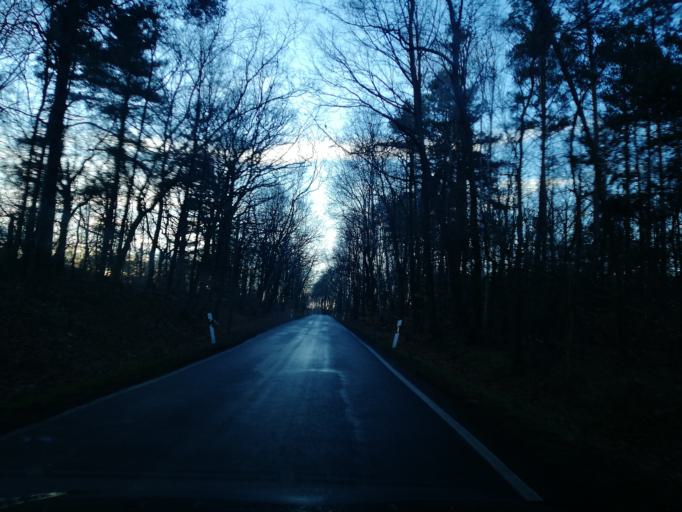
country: DE
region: Brandenburg
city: Calau
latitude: 51.7204
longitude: 13.9395
